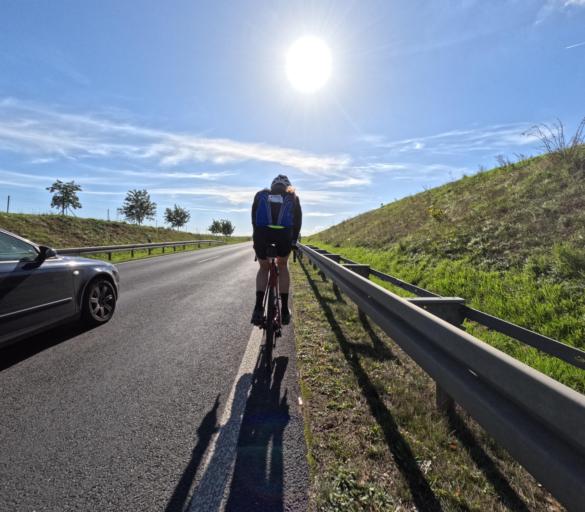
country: DE
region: Saxony
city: Moritzburg
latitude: 51.1444
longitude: 13.6503
